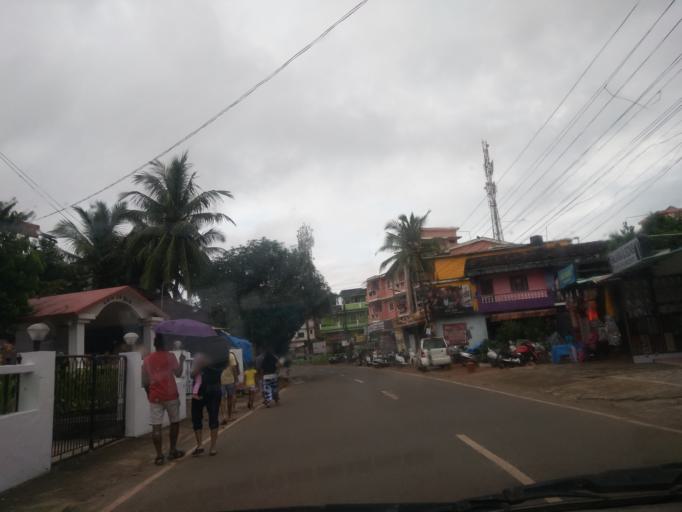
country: IN
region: Goa
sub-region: South Goa
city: Colva
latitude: 15.2766
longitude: 73.9197
